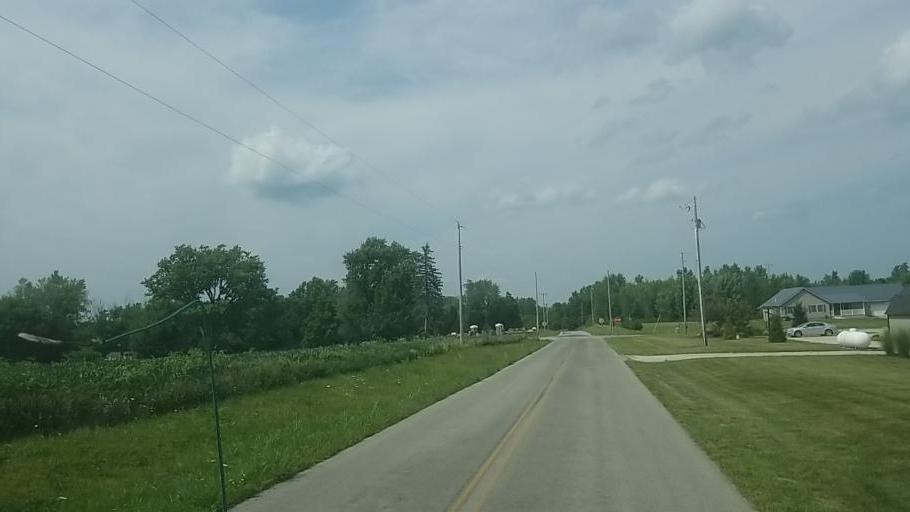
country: US
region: Ohio
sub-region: Hardin County
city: Forest
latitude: 40.8029
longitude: -83.5524
